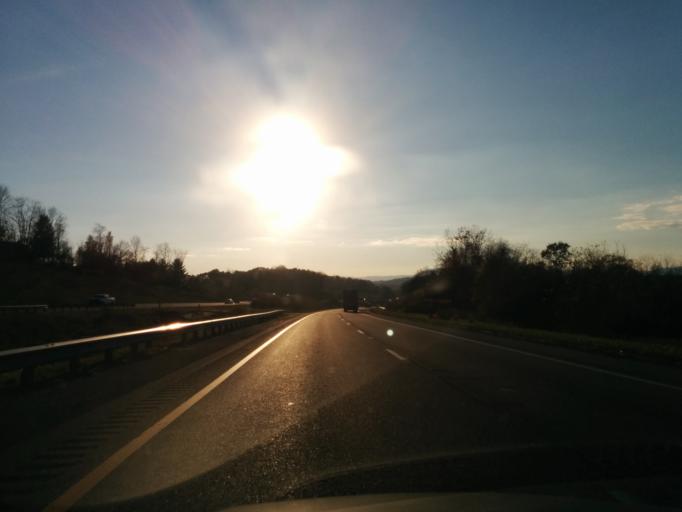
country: US
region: Virginia
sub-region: Rockbridge County
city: East Lexington
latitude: 37.8717
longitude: -79.3169
